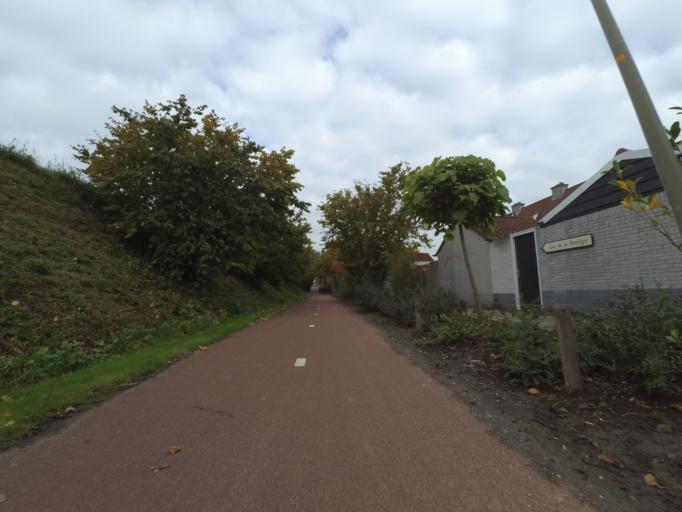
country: NL
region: Gelderland
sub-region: Gemeente Nijkerk
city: Nijkerk
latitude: 52.2215
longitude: 5.4720
